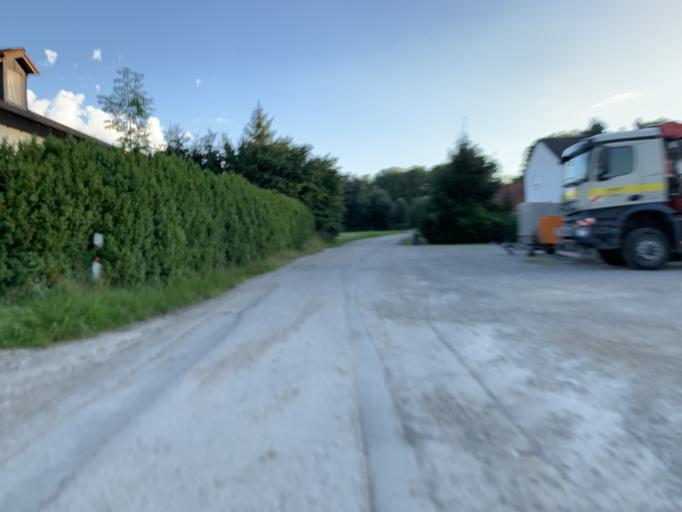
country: DE
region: Bavaria
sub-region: Upper Bavaria
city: Freising
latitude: 48.3815
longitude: 11.7460
